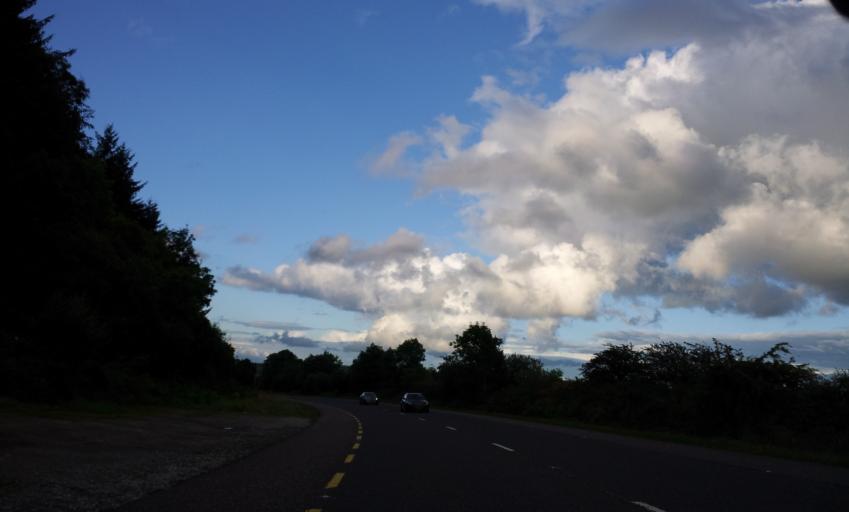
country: IE
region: Munster
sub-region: Ciarrai
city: Castleisland
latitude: 52.2996
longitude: -9.3849
